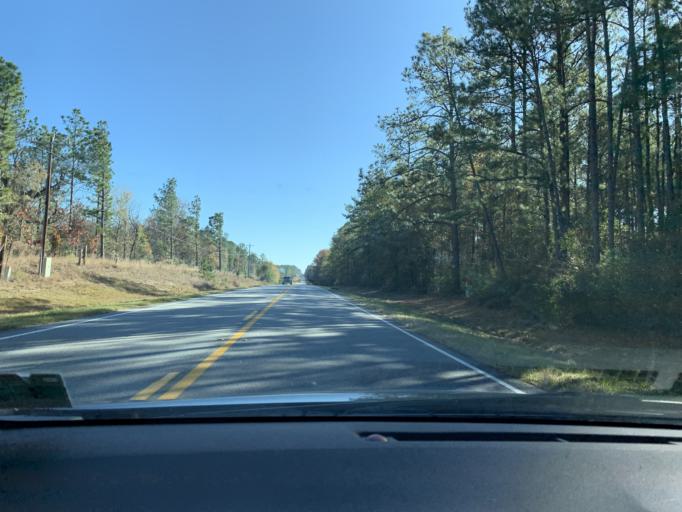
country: US
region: Georgia
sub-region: Ben Hill County
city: Fitzgerald
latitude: 31.7747
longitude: -83.0589
